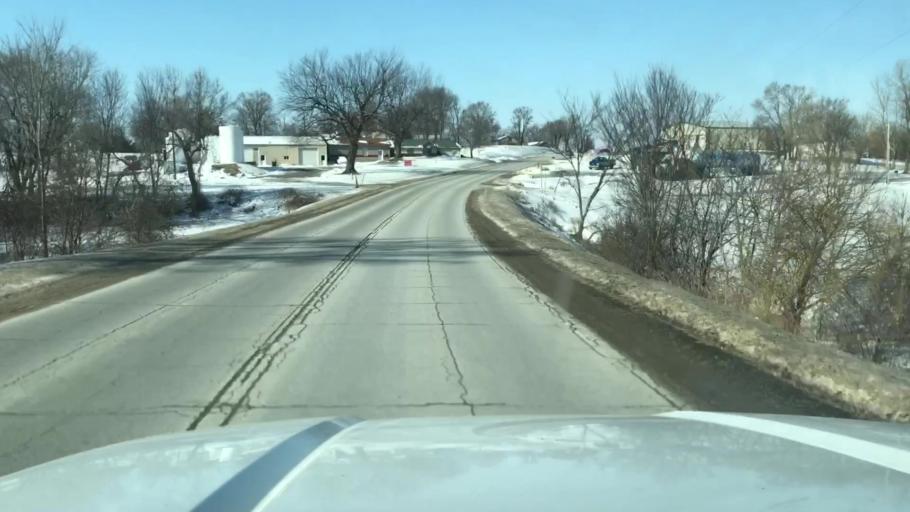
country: US
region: Missouri
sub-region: Andrew County
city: Savannah
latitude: 39.9471
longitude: -94.8384
